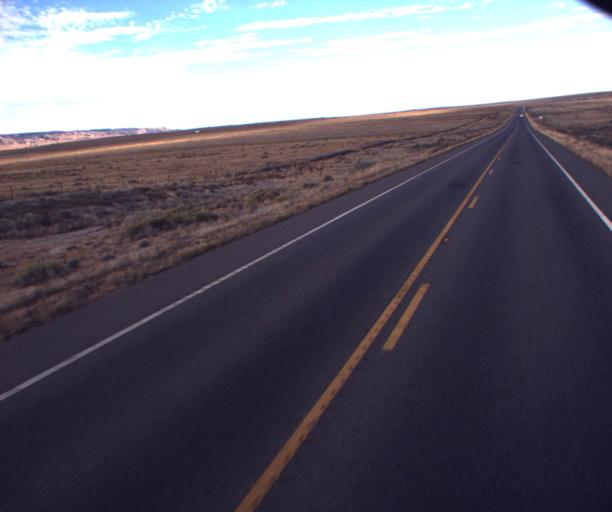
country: US
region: Arizona
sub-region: Apache County
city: Lukachukai
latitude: 36.9506
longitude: -109.2832
